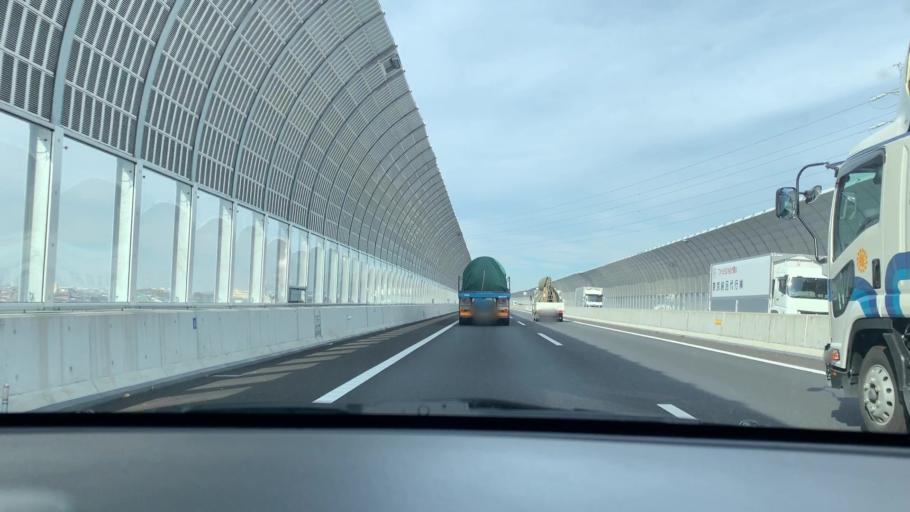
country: JP
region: Chiba
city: Matsudo
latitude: 35.7979
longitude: 139.8781
